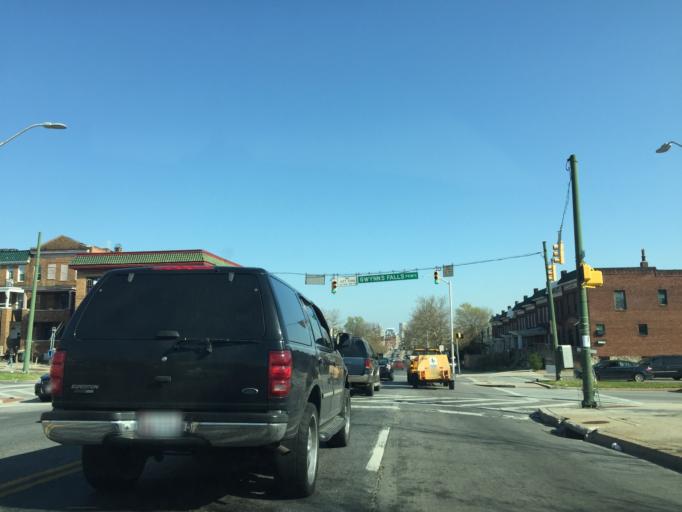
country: US
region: Maryland
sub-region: City of Baltimore
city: Baltimore
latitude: 39.3170
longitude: -76.6509
